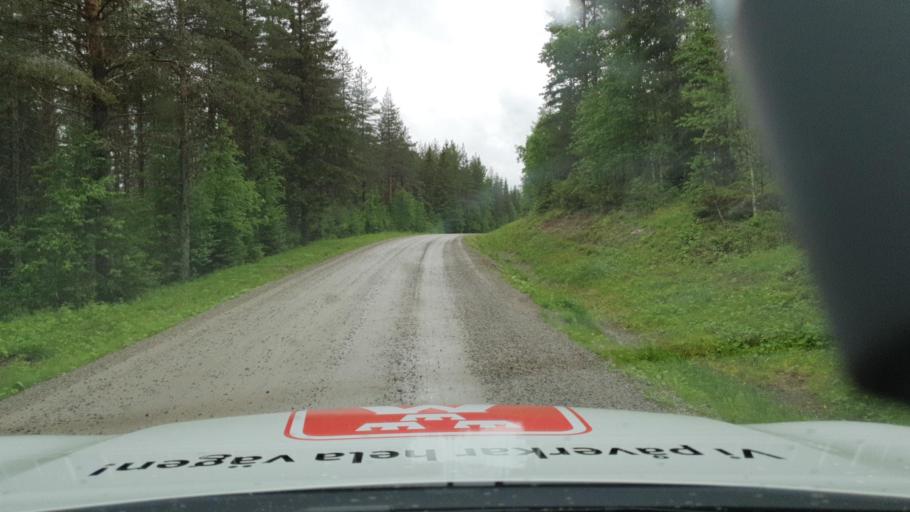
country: SE
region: Vaesterbotten
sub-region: Dorotea Kommun
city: Dorotea
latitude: 64.0452
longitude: 16.7396
